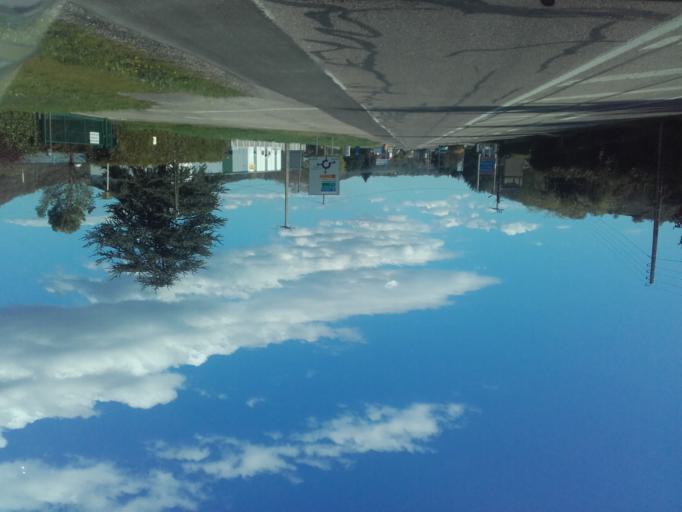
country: FR
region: Rhone-Alpes
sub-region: Departement de l'Isere
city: Nivolas-Vermelle
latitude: 45.5701
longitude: 5.3022
